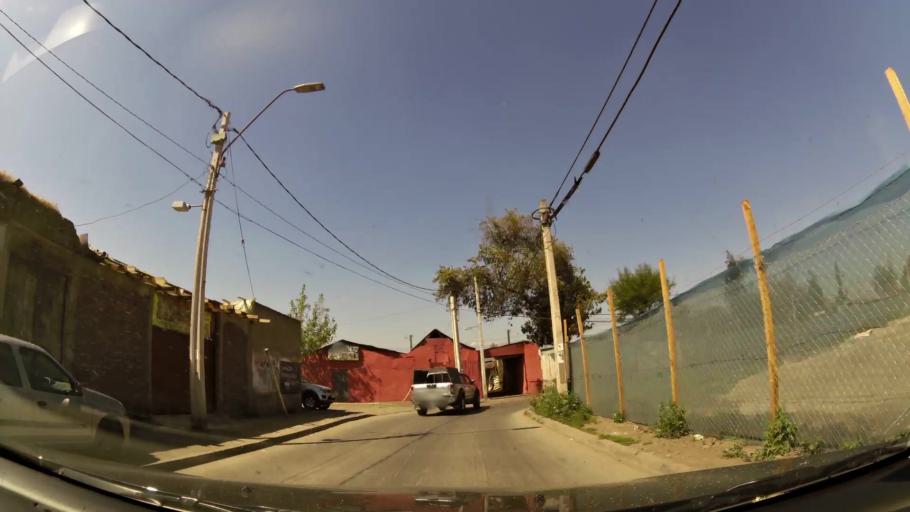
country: CL
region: Santiago Metropolitan
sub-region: Provincia de Santiago
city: Lo Prado
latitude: -33.4033
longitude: -70.7347
